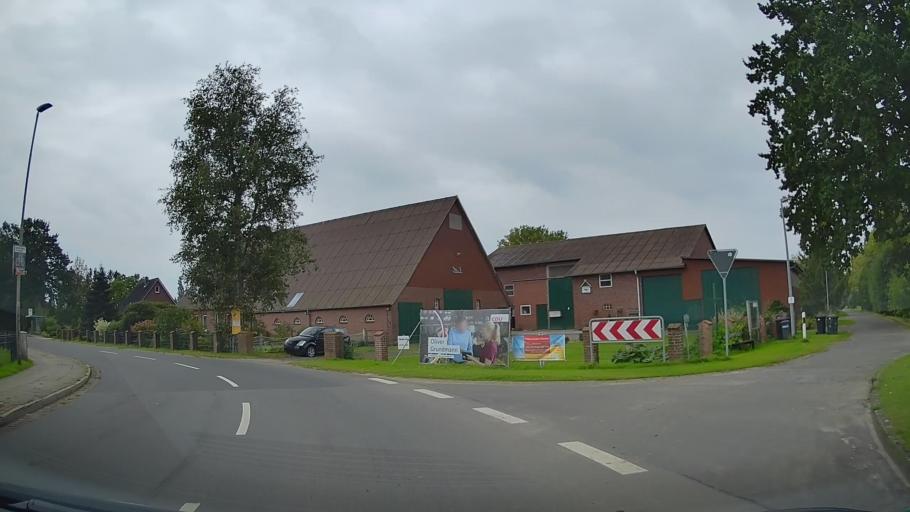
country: DE
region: Lower Saxony
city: Stade
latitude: 53.6355
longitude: 9.4637
